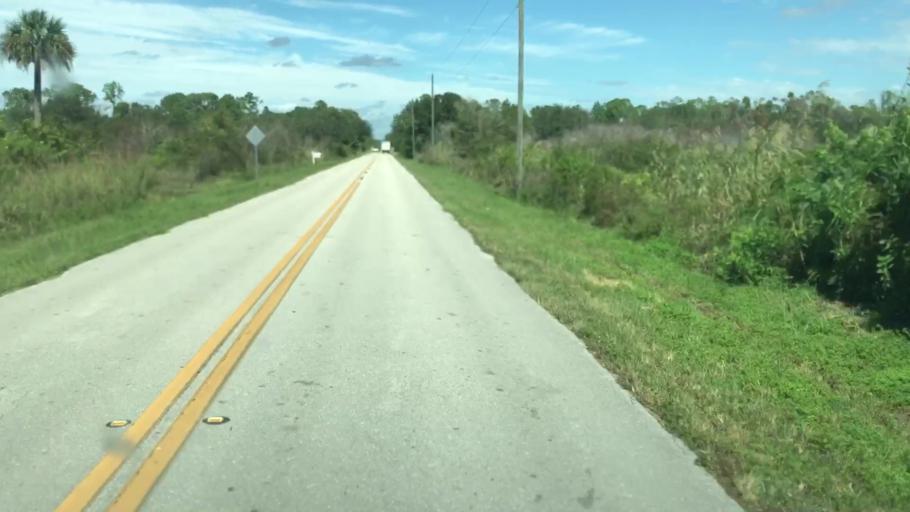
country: US
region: Florida
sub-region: Lee County
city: Lehigh Acres
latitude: 26.6514
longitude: -81.6465
